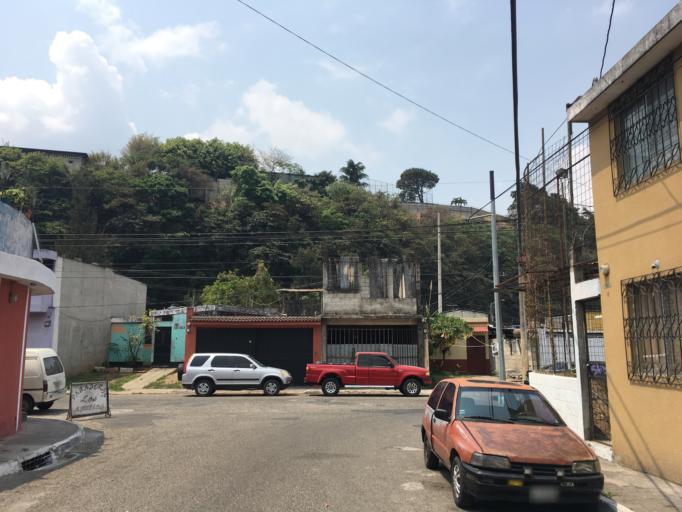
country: GT
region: Guatemala
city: Petapa
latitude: 14.5233
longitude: -90.5390
